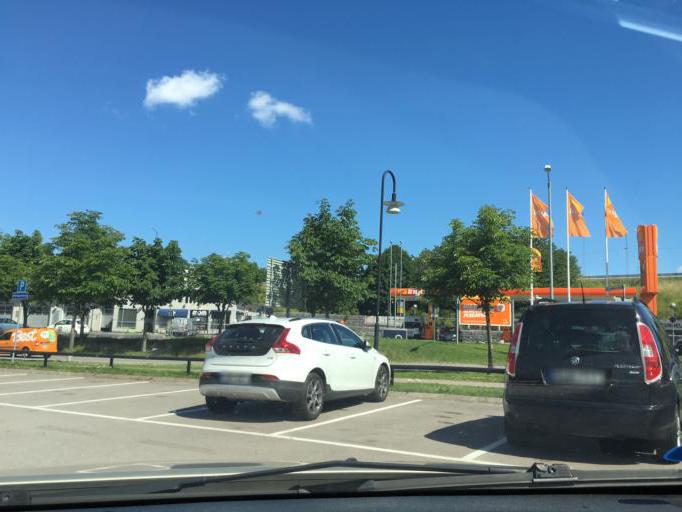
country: SE
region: Stockholm
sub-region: Nacka Kommun
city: Nacka
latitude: 59.3116
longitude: 18.1762
